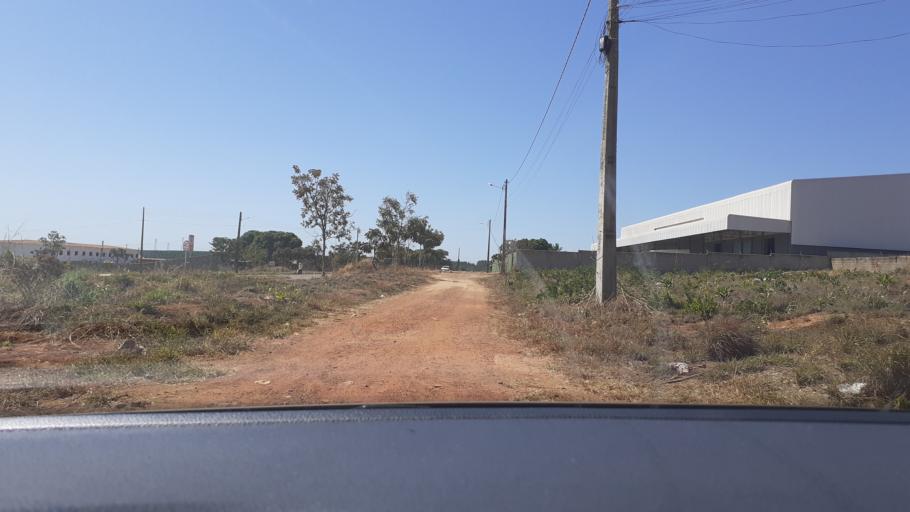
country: BR
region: Goias
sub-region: Aparecida De Goiania
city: Aparecida de Goiania
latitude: -16.8797
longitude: -49.2557
